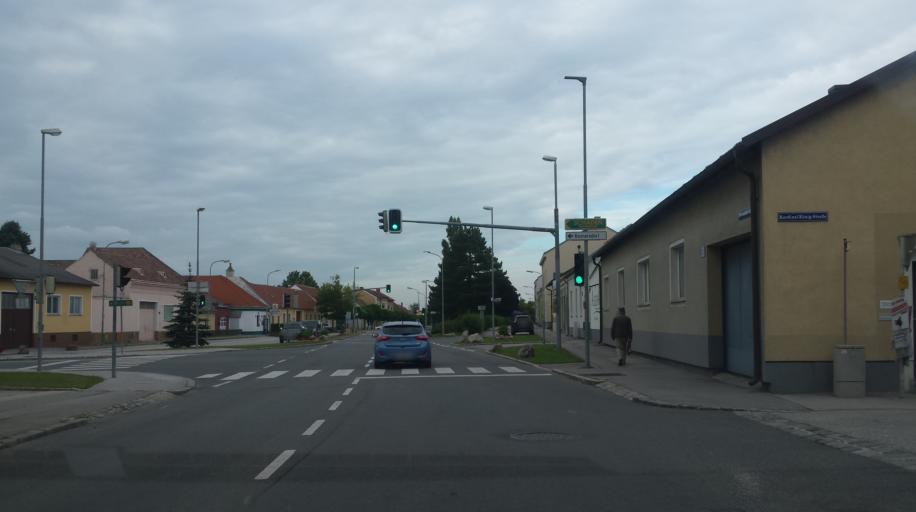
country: AT
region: Lower Austria
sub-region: Politischer Bezirk Wien-Umgebung
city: Zwolfaxing
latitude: 48.1097
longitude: 16.4623
